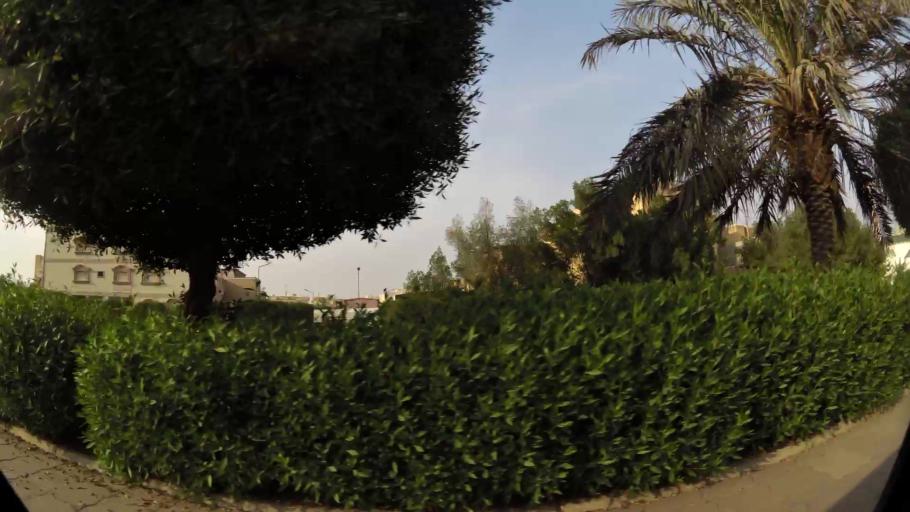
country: KW
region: Mubarak al Kabir
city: Mubarak al Kabir
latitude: 29.1830
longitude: 48.0756
